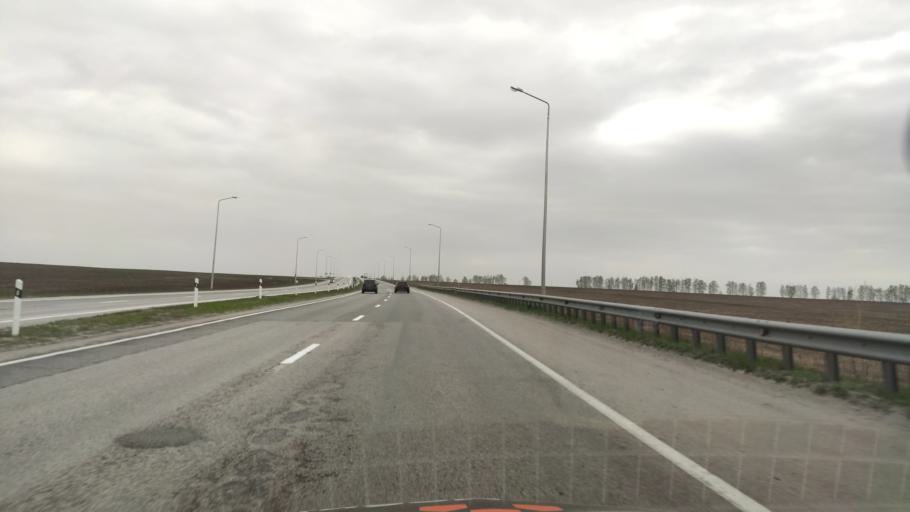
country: RU
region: Belgorod
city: Staryy Oskol
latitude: 51.3369
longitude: 37.7657
